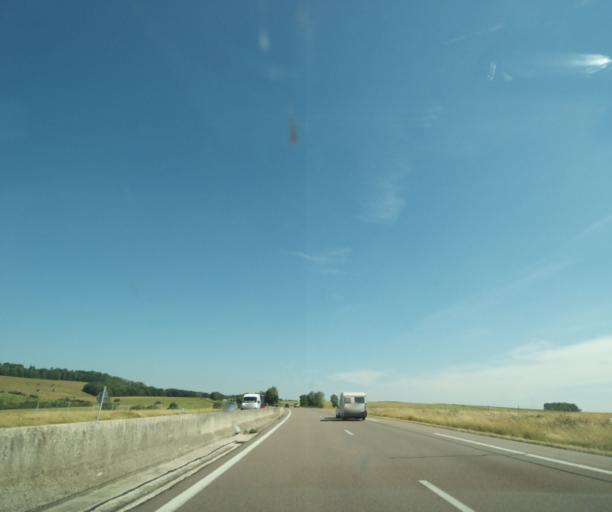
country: FR
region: Lorraine
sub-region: Departement des Vosges
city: Chatenois
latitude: 48.3812
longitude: 5.8822
